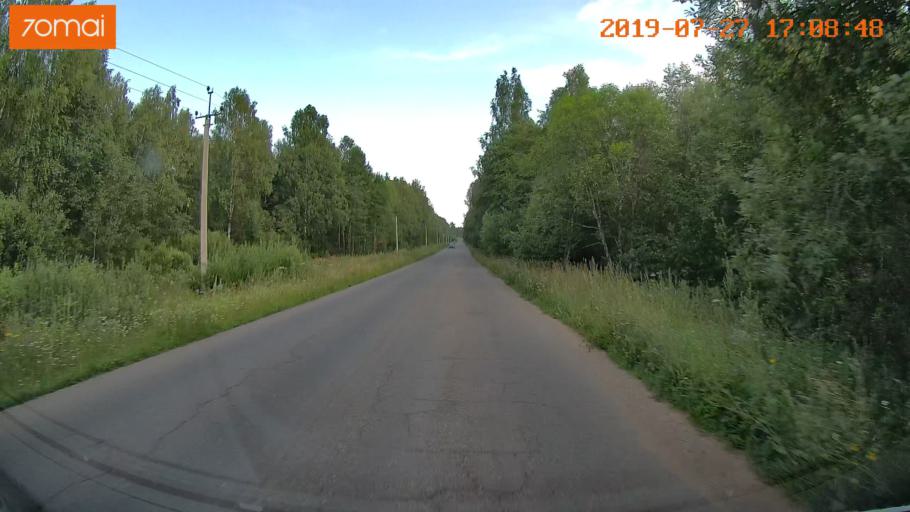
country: RU
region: Ivanovo
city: Novo-Talitsy
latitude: 57.0797
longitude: 40.8416
